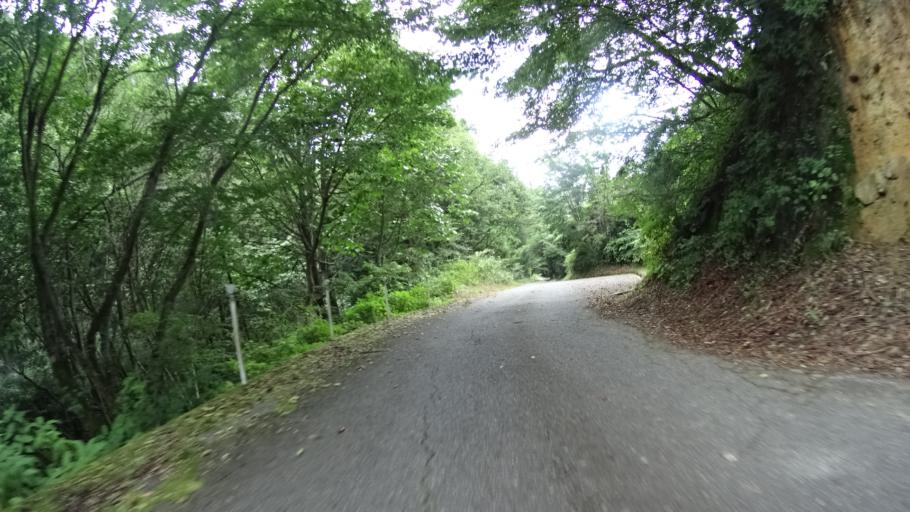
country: JP
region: Yamanashi
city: Nirasaki
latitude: 35.7982
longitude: 138.5281
